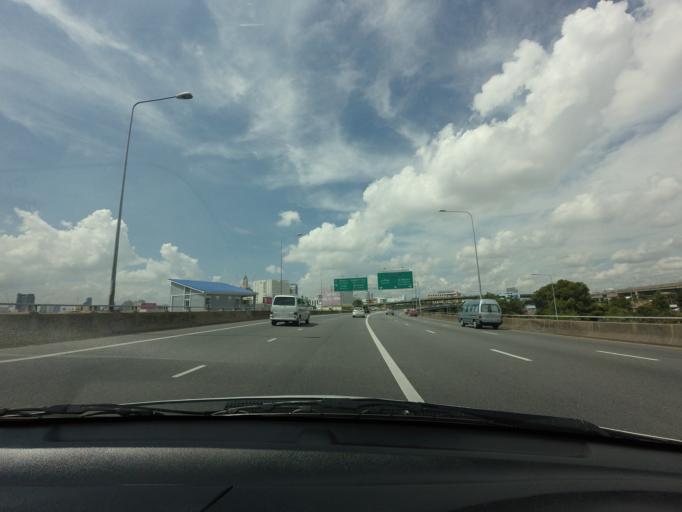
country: TH
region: Bangkok
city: Phaya Thai
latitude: 13.7752
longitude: 100.5328
